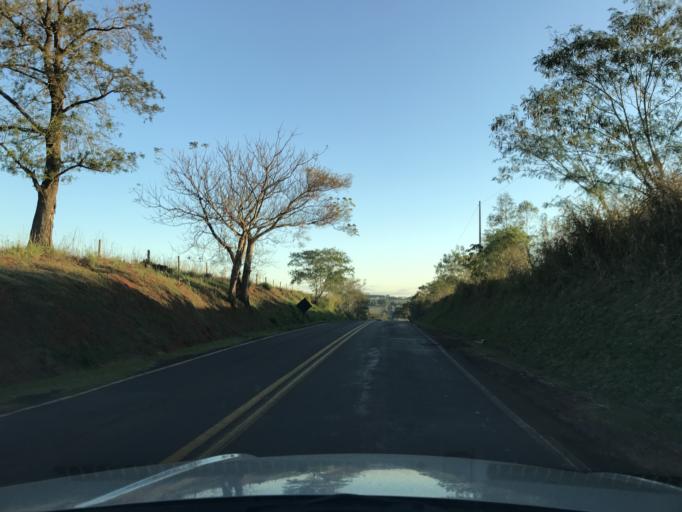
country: PY
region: Canindeyu
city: Salto del Guaira
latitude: -24.0890
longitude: -54.0926
